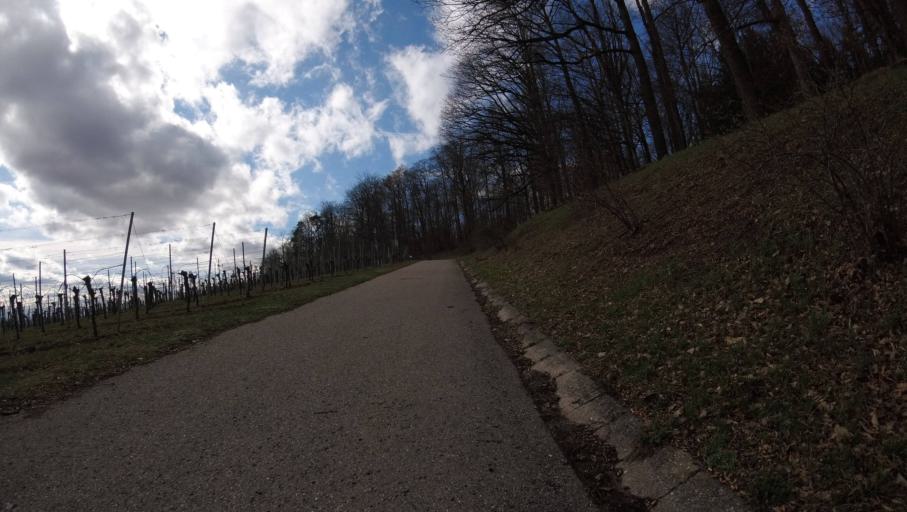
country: DE
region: Baden-Wuerttemberg
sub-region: Regierungsbezirk Stuttgart
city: Grossbottwar
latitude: 48.9941
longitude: 9.3192
